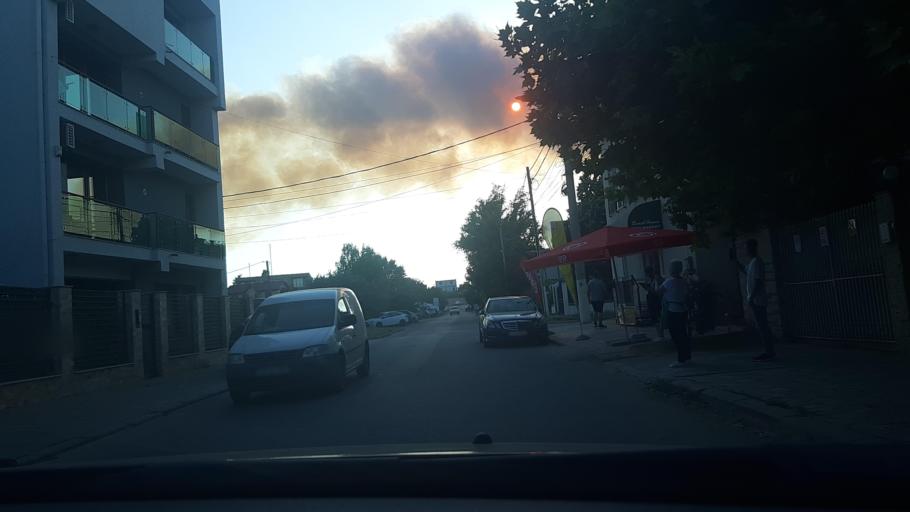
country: RO
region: Constanta
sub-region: Comuna Navodari
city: Navodari
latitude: 44.3001
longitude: 28.6229
